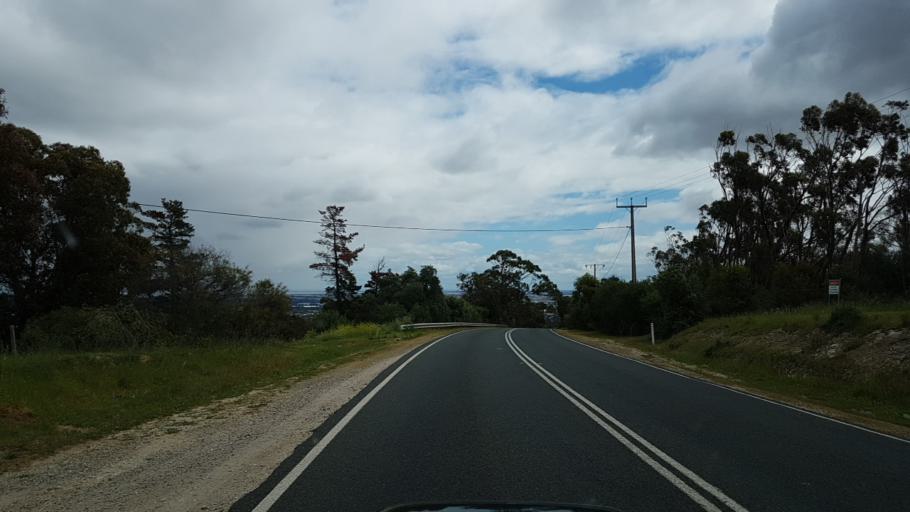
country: AU
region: South Australia
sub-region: Salisbury
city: Elizabeth
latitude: -34.7436
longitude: 138.6996
